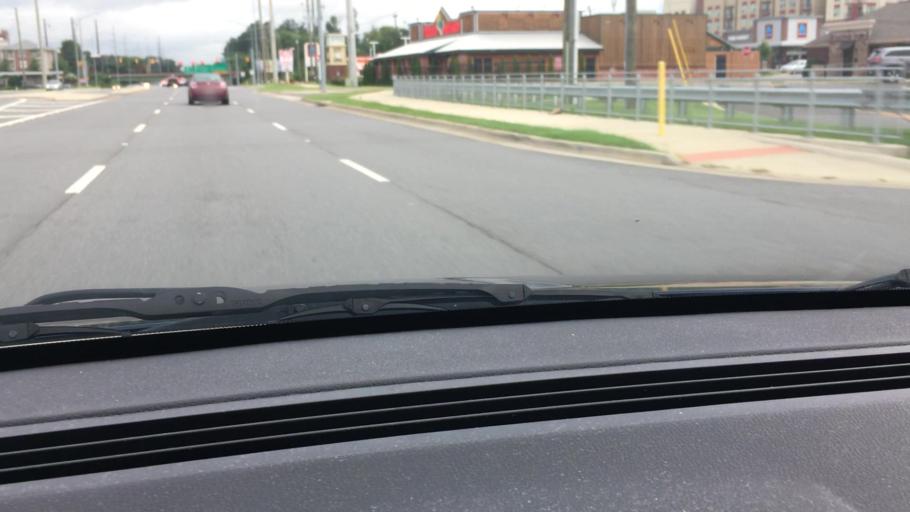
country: US
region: Alabama
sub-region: Tuscaloosa County
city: Tuscaloosa
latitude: 33.1984
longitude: -87.5257
